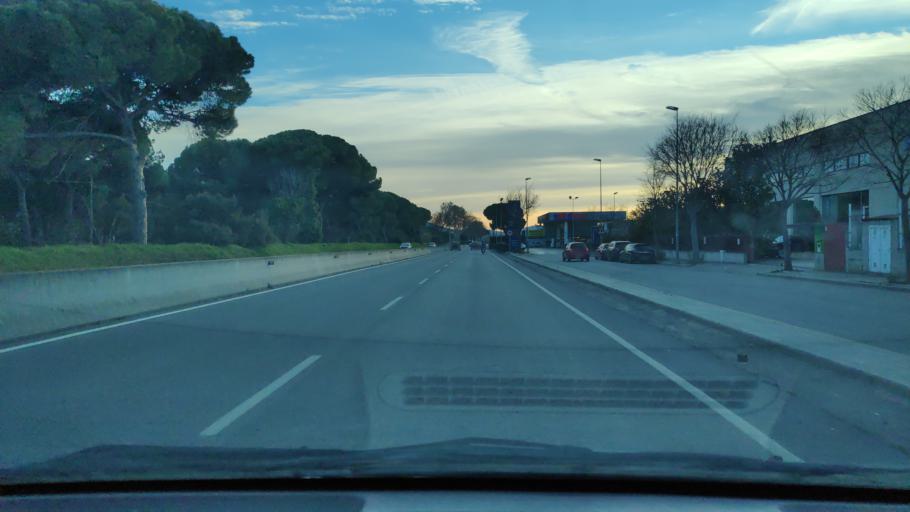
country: ES
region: Catalonia
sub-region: Provincia de Barcelona
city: Montmelo
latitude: 41.5706
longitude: 2.2694
